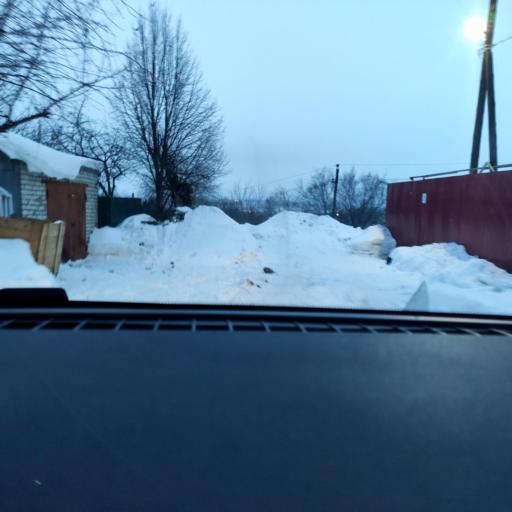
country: RU
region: Samara
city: Samara
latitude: 53.1738
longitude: 50.1640
